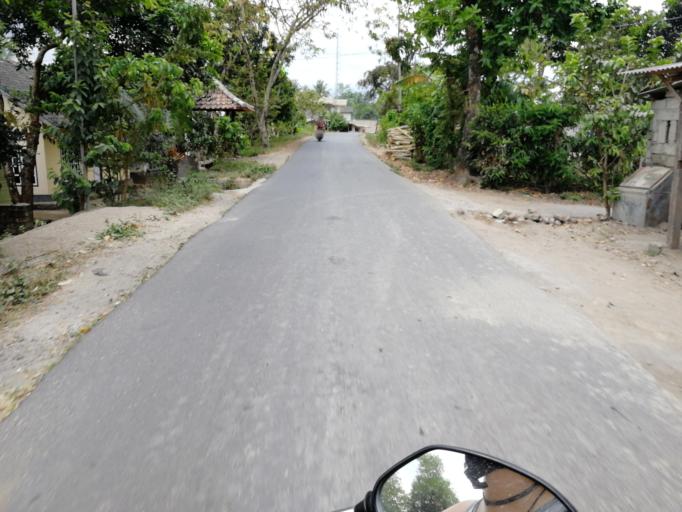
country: ID
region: West Nusa Tenggara
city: Pediti
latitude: -8.5685
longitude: 116.3300
